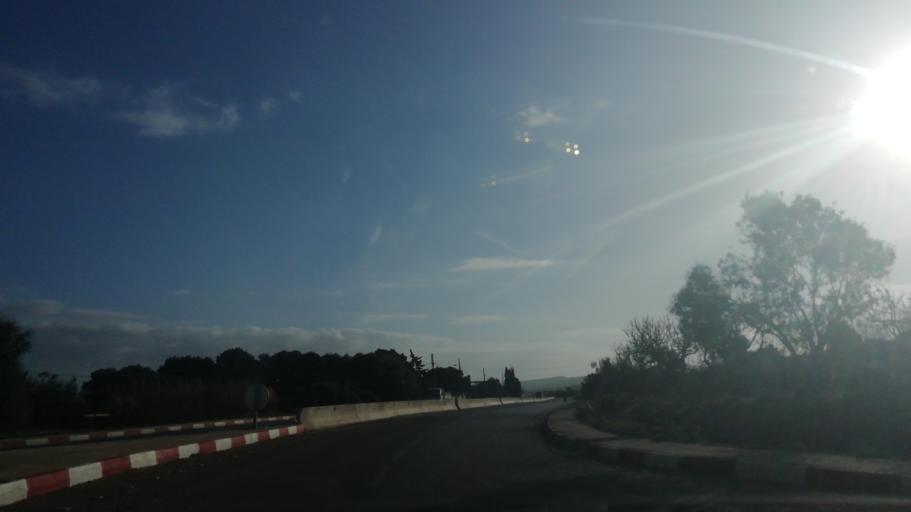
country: DZ
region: Mostaganem
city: Mostaganem
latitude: 36.1069
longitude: 0.3020
